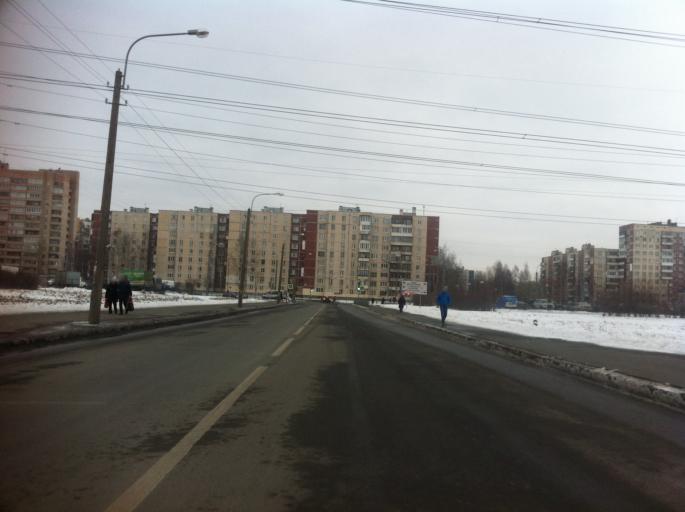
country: RU
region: St.-Petersburg
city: Uritsk
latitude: 59.8503
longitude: 30.1946
